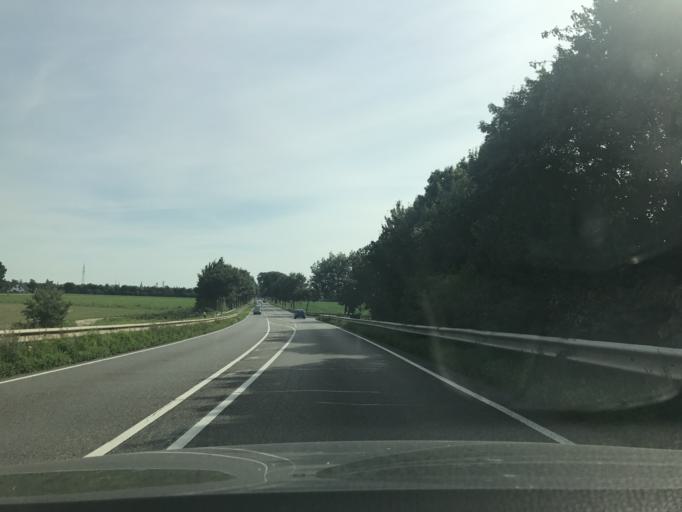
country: DE
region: North Rhine-Westphalia
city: Kempen
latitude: 51.3858
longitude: 6.4159
